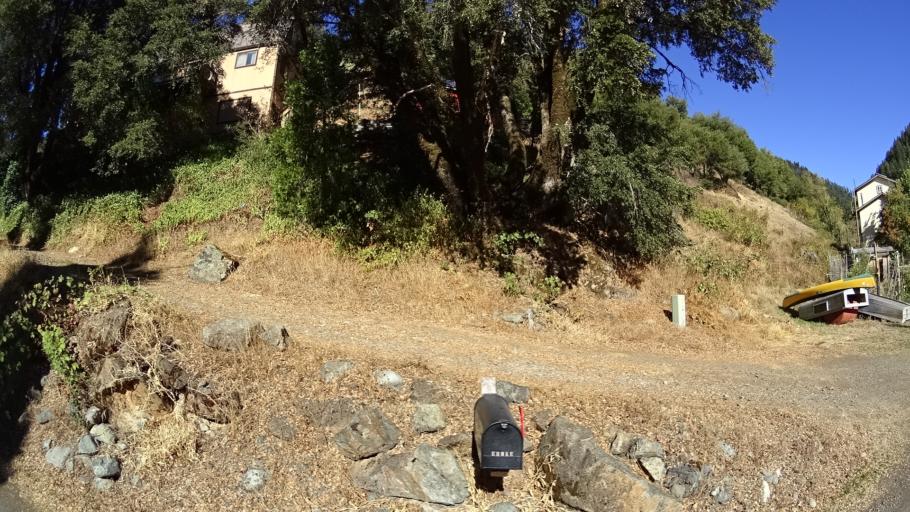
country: US
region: California
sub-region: Siskiyou County
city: Happy Camp
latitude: 41.2974
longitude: -123.1311
